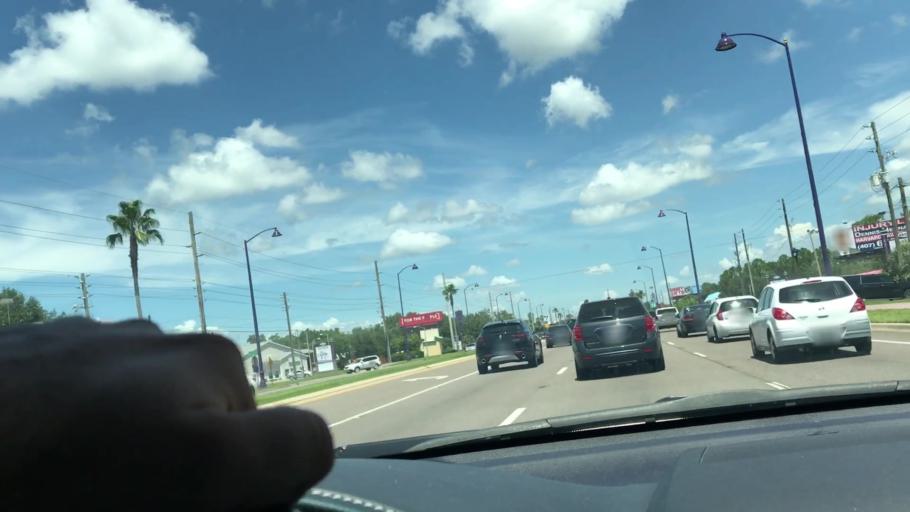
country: US
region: Florida
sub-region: Osceola County
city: Kissimmee
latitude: 28.3099
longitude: -81.4653
